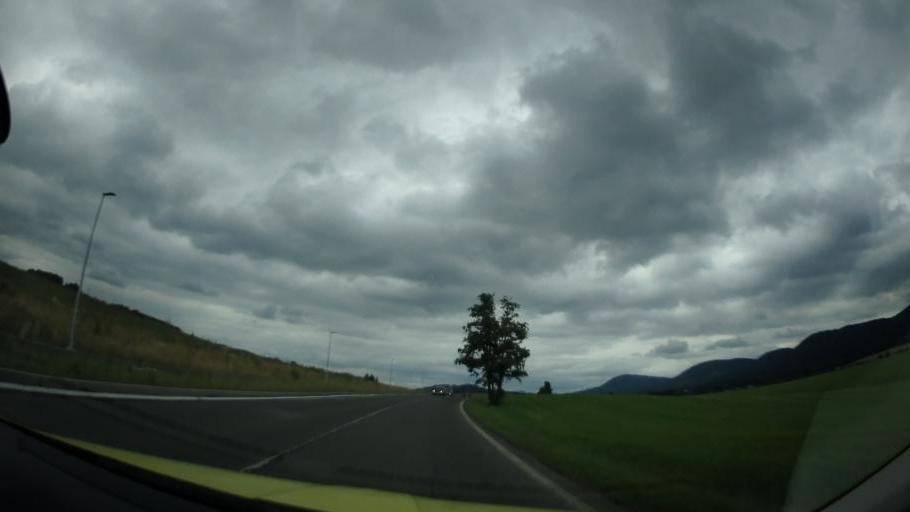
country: CZ
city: Morkov
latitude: 49.5379
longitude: 18.0474
